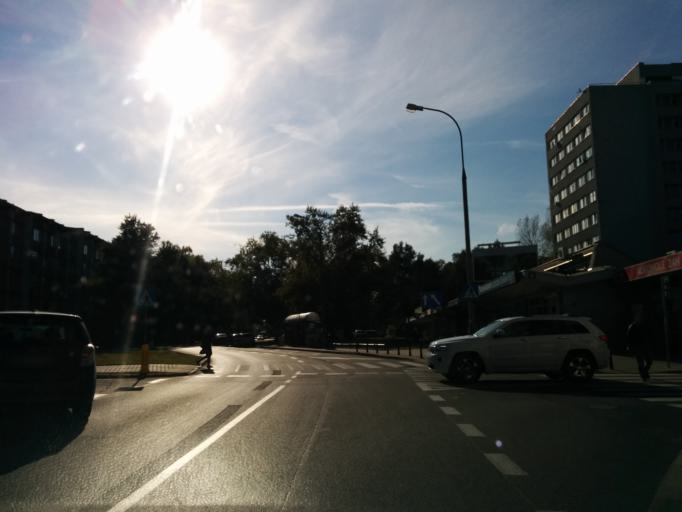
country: PL
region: Masovian Voivodeship
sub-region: Warszawa
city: Zoliborz
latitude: 52.2663
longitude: 20.9761
